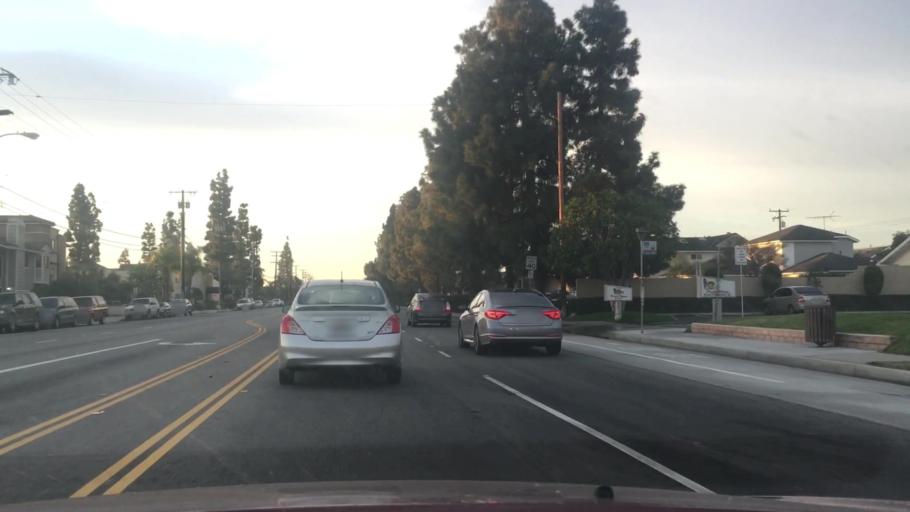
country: US
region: California
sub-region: Orange County
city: Stanton
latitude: 33.8098
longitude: -118.0108
